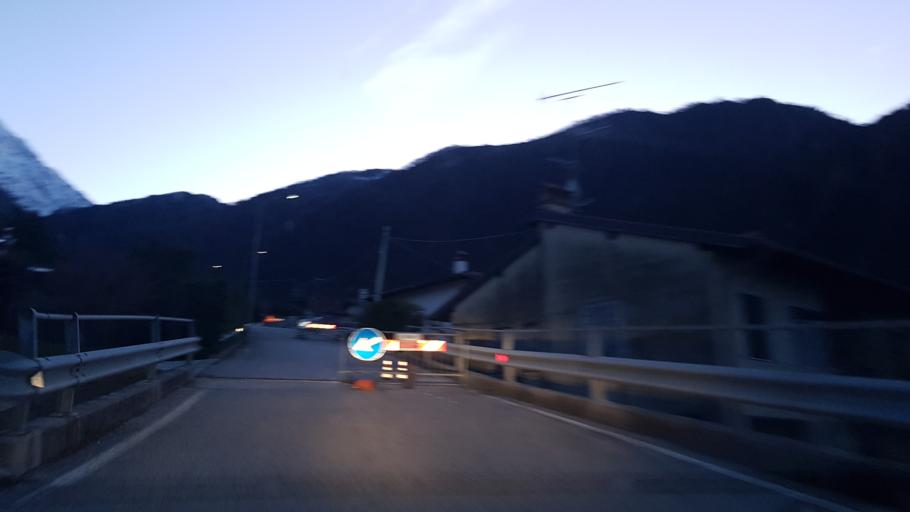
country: IT
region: Friuli Venezia Giulia
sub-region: Provincia di Udine
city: Gemona
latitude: 46.2814
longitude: 13.1423
